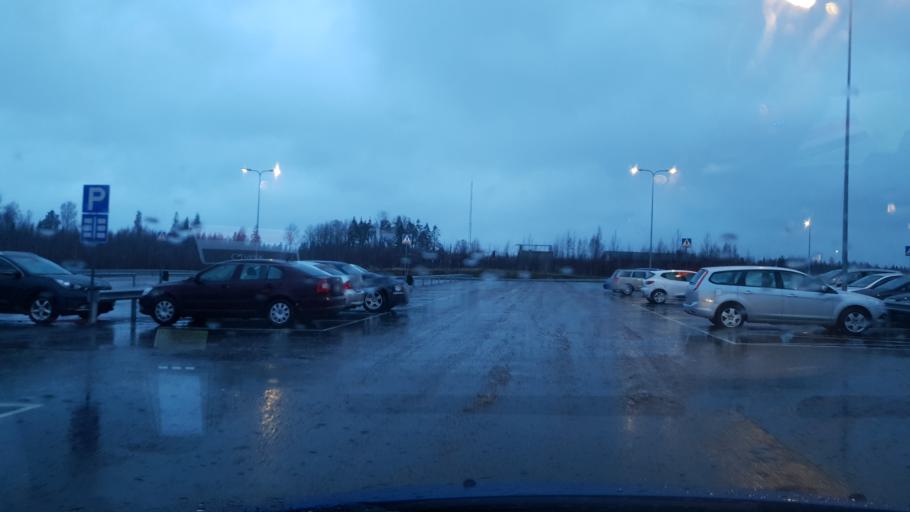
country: FI
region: Uusimaa
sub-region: Helsinki
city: Kerava
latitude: 60.3766
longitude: 25.1518
